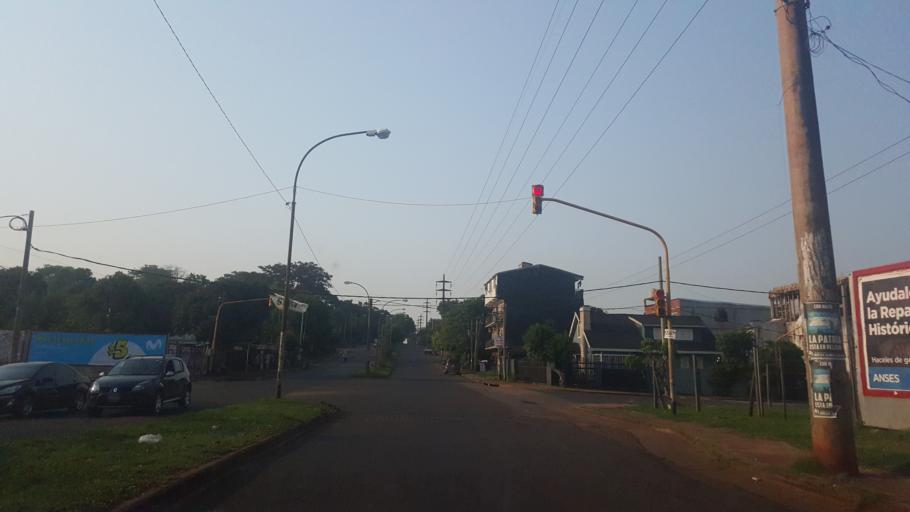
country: AR
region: Misiones
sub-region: Departamento de Capital
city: Posadas
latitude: -27.3922
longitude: -55.8934
